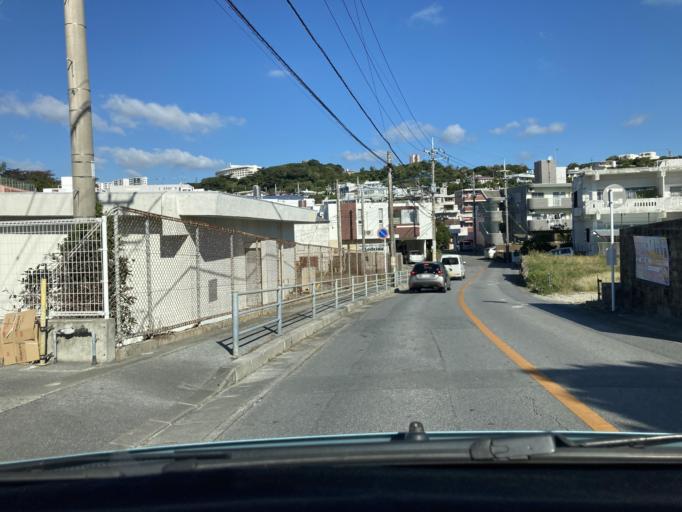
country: JP
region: Okinawa
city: Chatan
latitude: 26.2999
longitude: 127.7975
